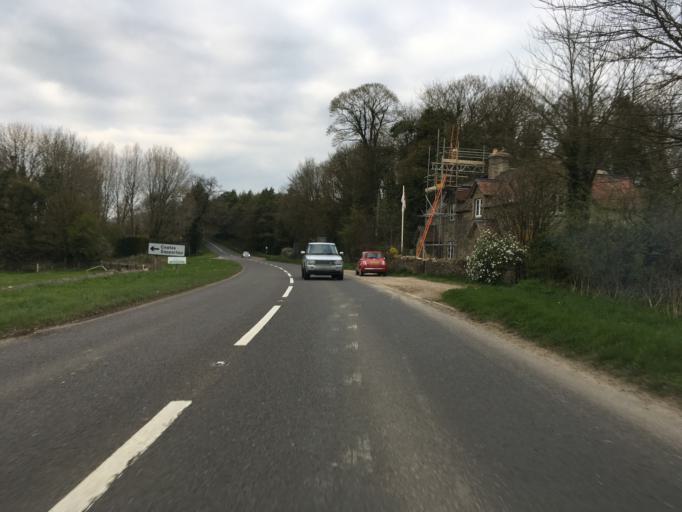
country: GB
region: England
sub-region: Gloucestershire
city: Coates
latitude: 51.6877
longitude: -2.0045
